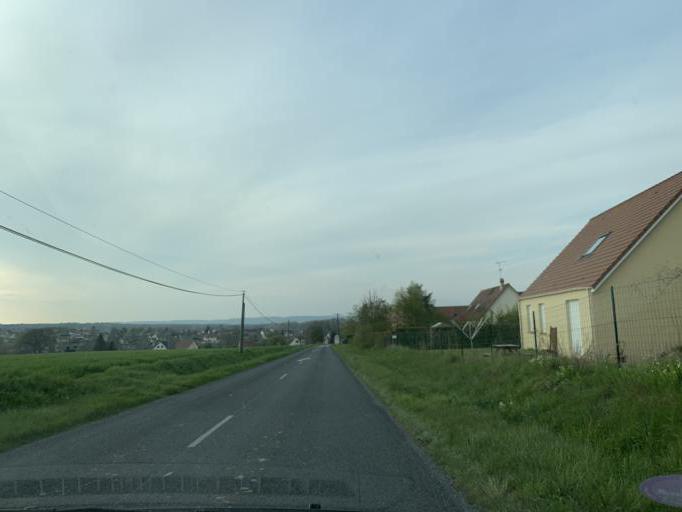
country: FR
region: Haute-Normandie
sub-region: Departement de la Seine-Maritime
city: La Mailleraye-sur-Seine
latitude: 49.4719
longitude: 0.7747
